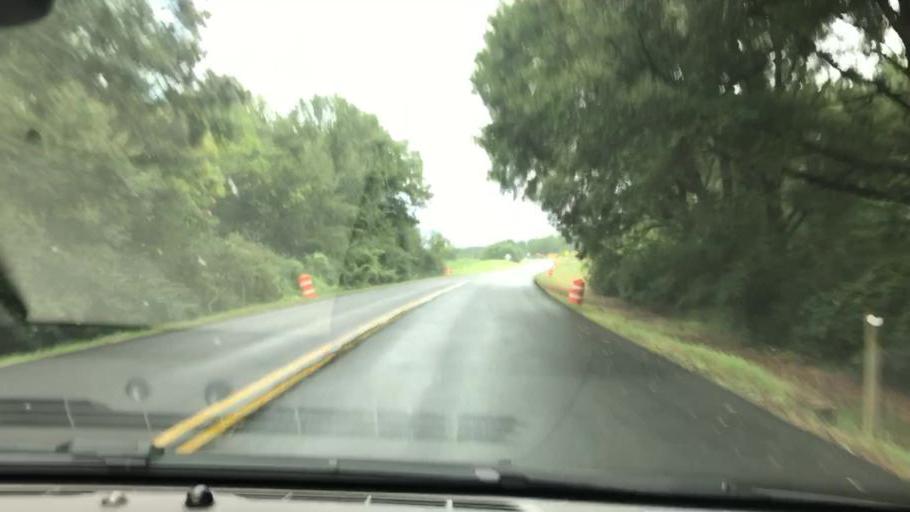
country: US
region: Georgia
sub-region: Early County
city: Blakely
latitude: 31.4072
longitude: -84.9613
